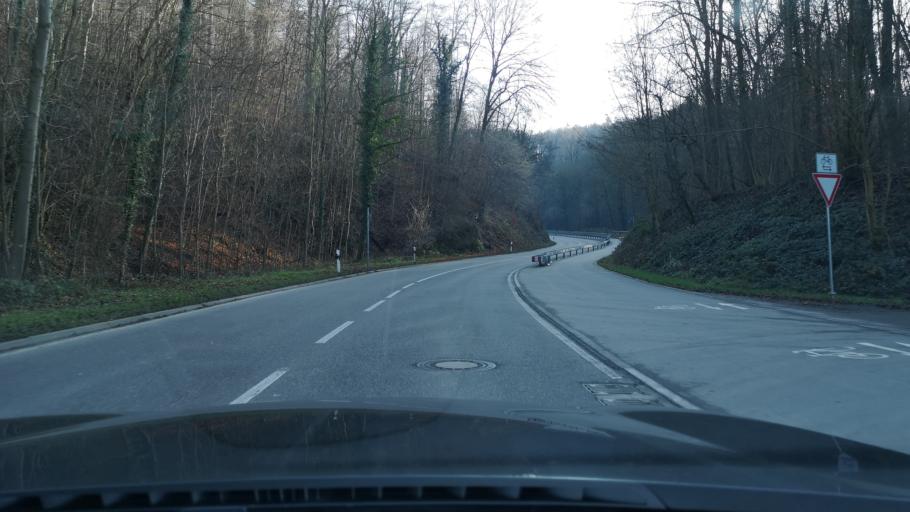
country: DE
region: Baden-Wuerttemberg
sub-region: Karlsruhe Region
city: Karlsruhe
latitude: 48.9804
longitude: 8.4650
